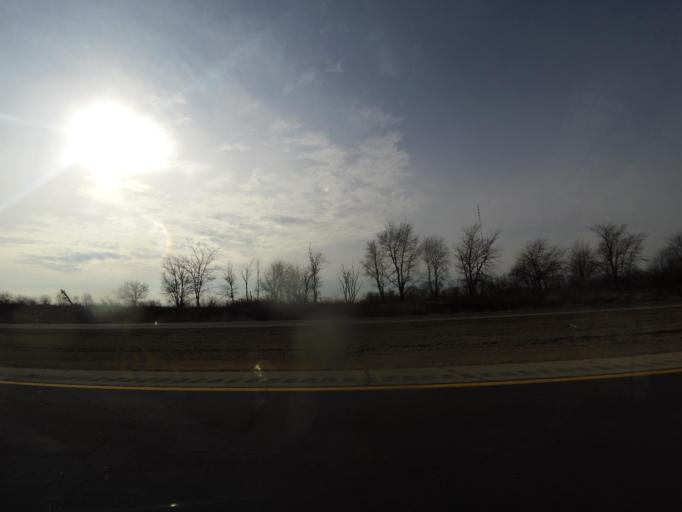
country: US
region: Illinois
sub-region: Macon County
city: Decatur
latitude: 39.7886
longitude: -88.9878
